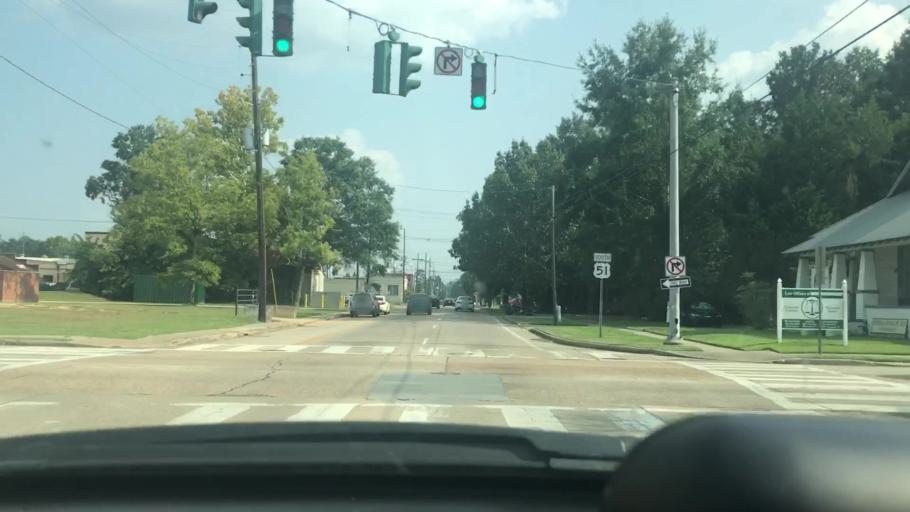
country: US
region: Louisiana
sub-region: Tangipahoa Parish
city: Hammond
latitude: 30.5031
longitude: -90.4621
